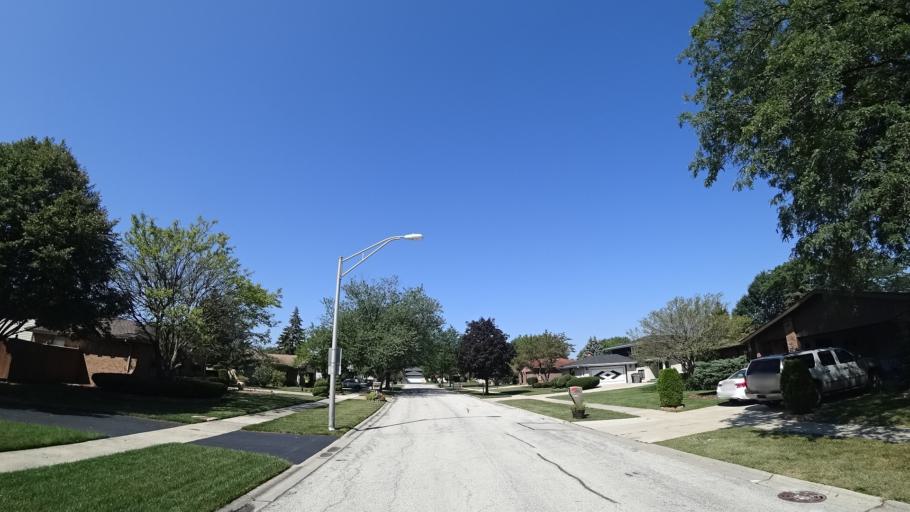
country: US
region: Illinois
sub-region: Cook County
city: Orland Park
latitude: 41.6346
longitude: -87.8253
